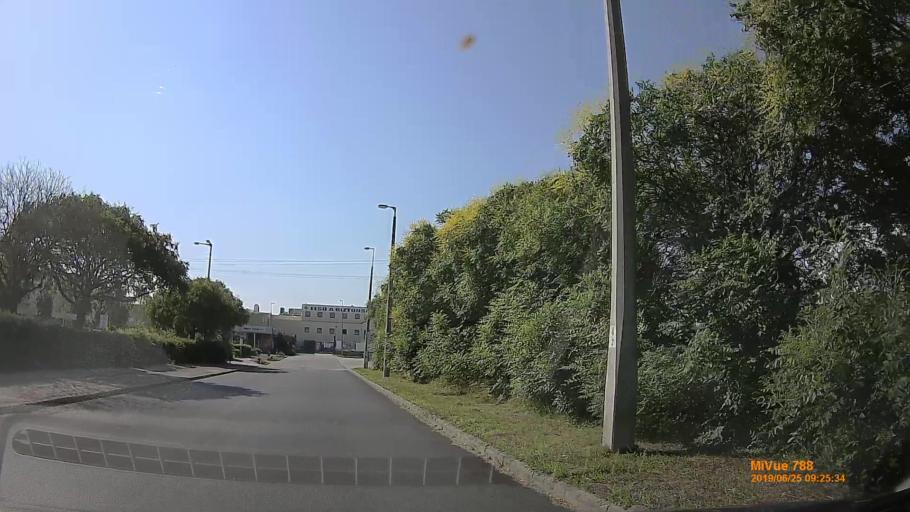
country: HU
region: Komarom-Esztergom
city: Esztergom
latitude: 47.7694
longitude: 18.7465
